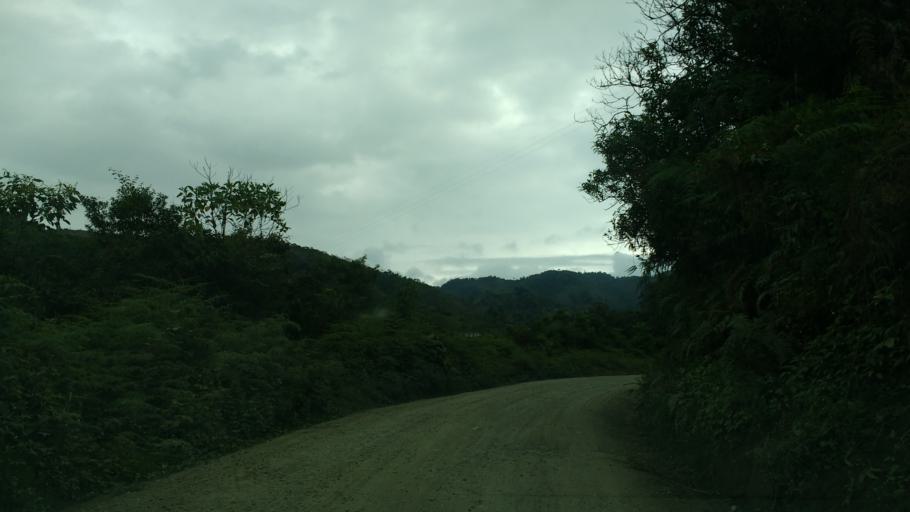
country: CO
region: Antioquia
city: Concepcion
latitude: 6.3308
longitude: -75.2904
